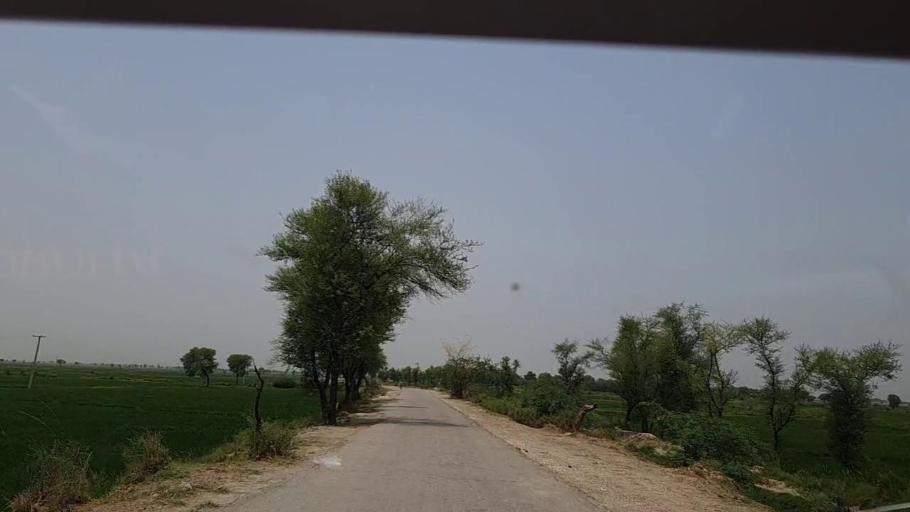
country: PK
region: Sindh
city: Khairpur Nathan Shah
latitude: 27.0064
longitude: 67.6710
